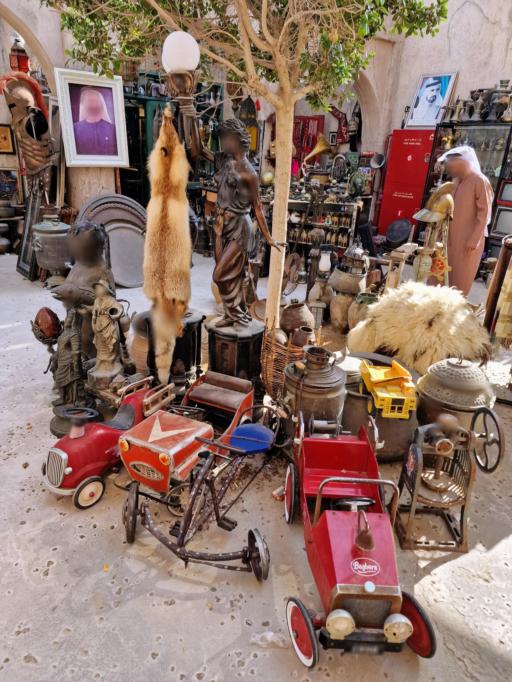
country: AE
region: Ash Shariqah
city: Sharjah
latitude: 25.2646
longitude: 55.3031
